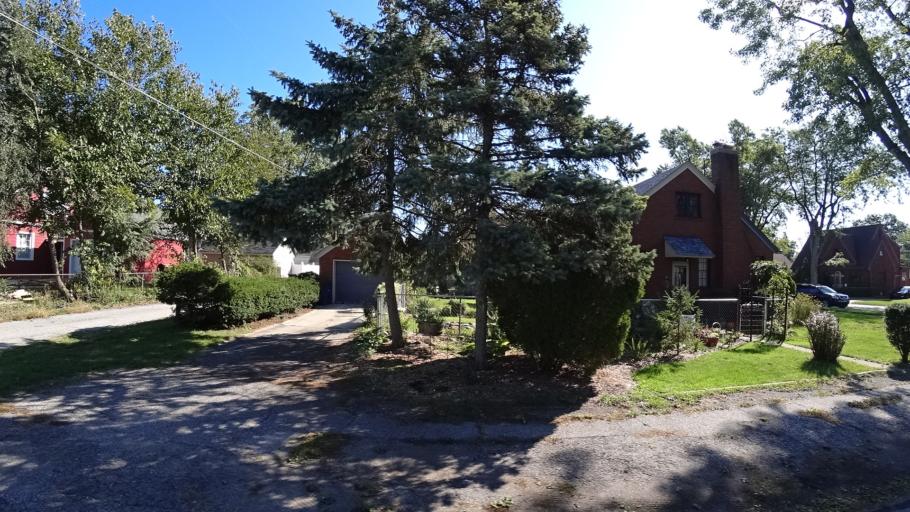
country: US
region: Indiana
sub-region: LaPorte County
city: Michigan City
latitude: 41.7093
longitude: -86.8908
